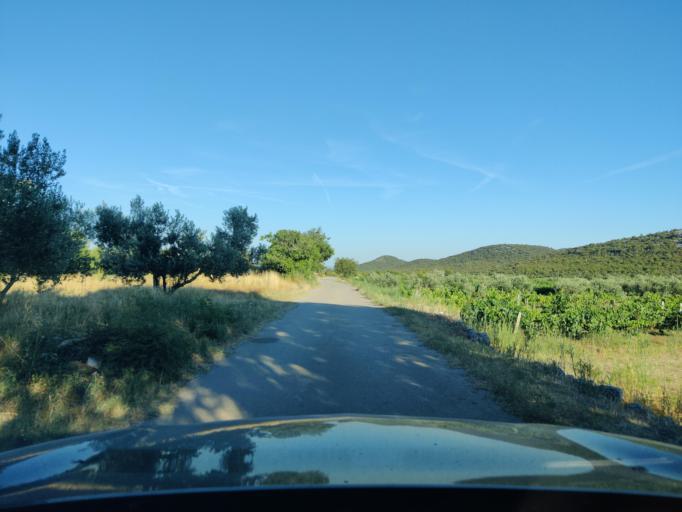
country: HR
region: Sibensko-Kniniska
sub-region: Grad Sibenik
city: Pirovac
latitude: 43.8623
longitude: 15.7021
